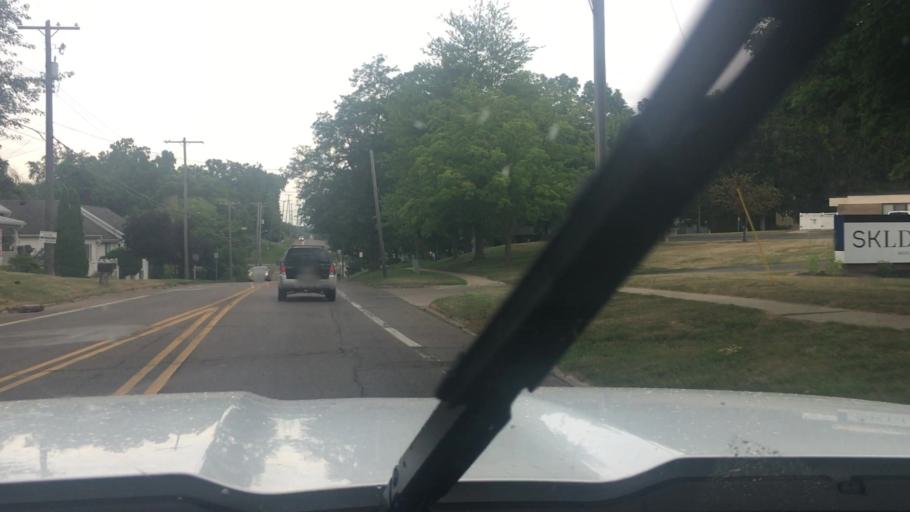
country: US
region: Michigan
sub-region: Ionia County
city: Ionia
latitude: 42.9874
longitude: -85.0453
